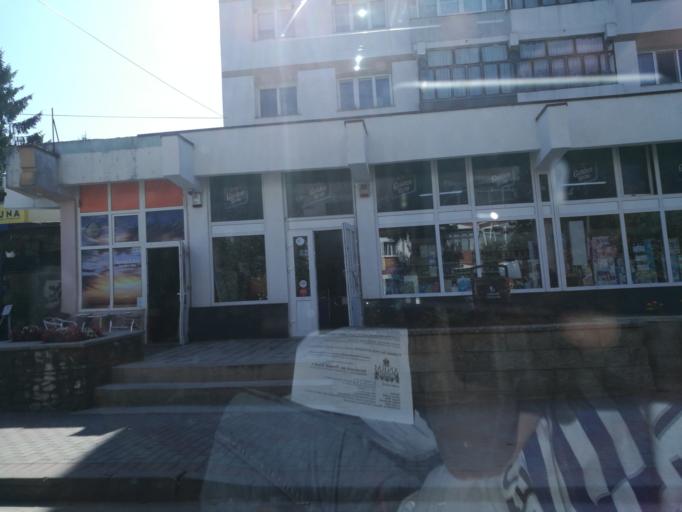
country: RO
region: Suceava
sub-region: Municipiul Suceava
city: Radauti
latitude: 47.8364
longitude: 25.9286
